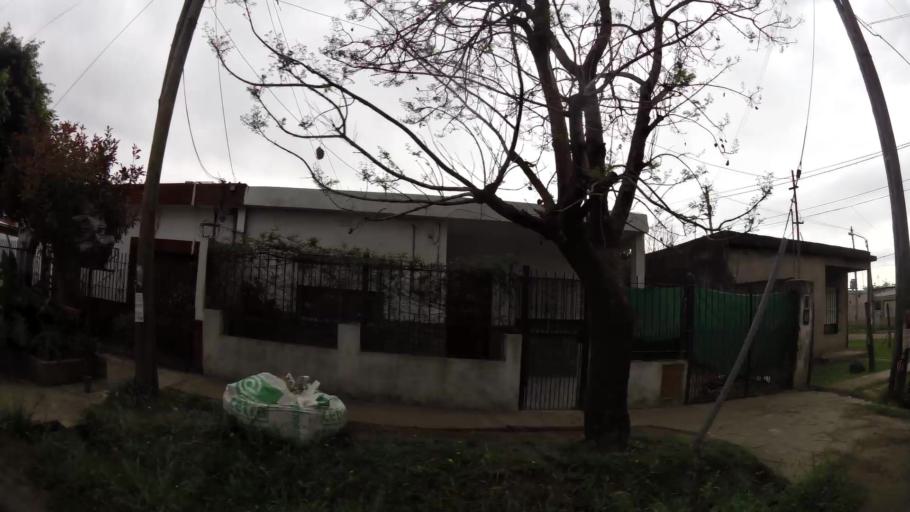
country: AR
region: Buenos Aires
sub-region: Partido de Quilmes
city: Quilmes
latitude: -34.7949
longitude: -58.2694
